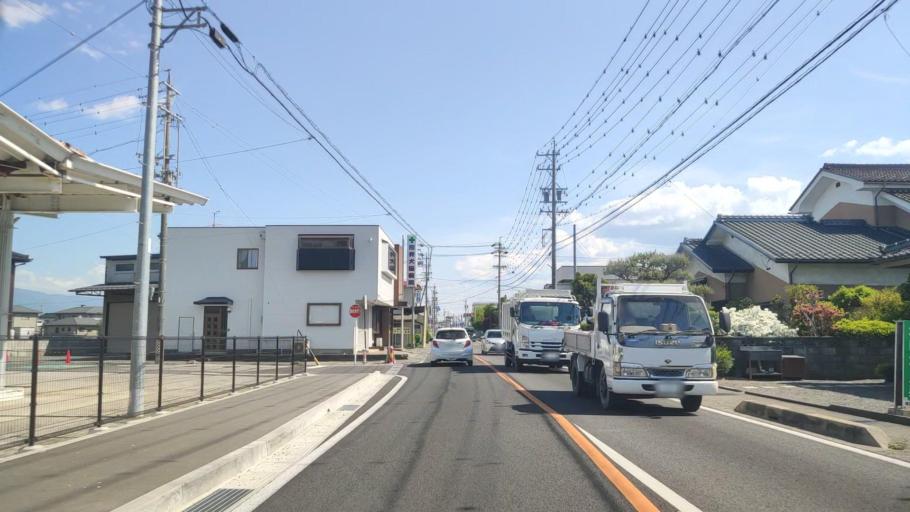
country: JP
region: Nagano
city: Toyoshina
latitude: 36.2908
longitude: 137.9070
